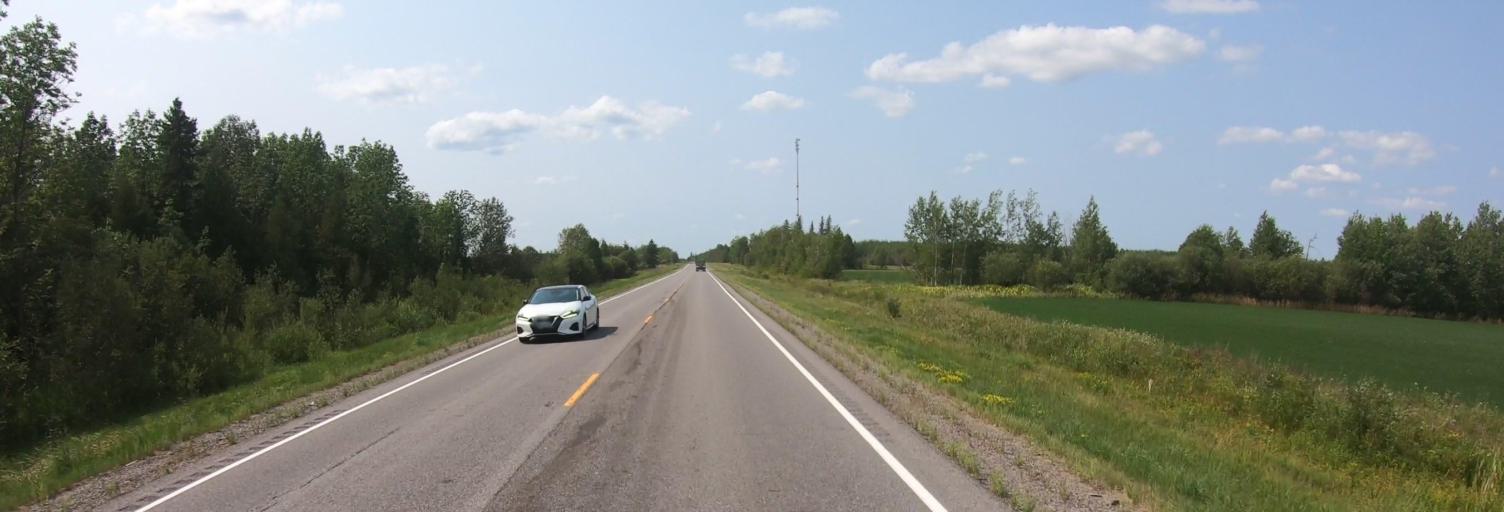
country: US
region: Minnesota
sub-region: Lake of the Woods County
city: Baudette
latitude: 48.6285
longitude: -94.0120
